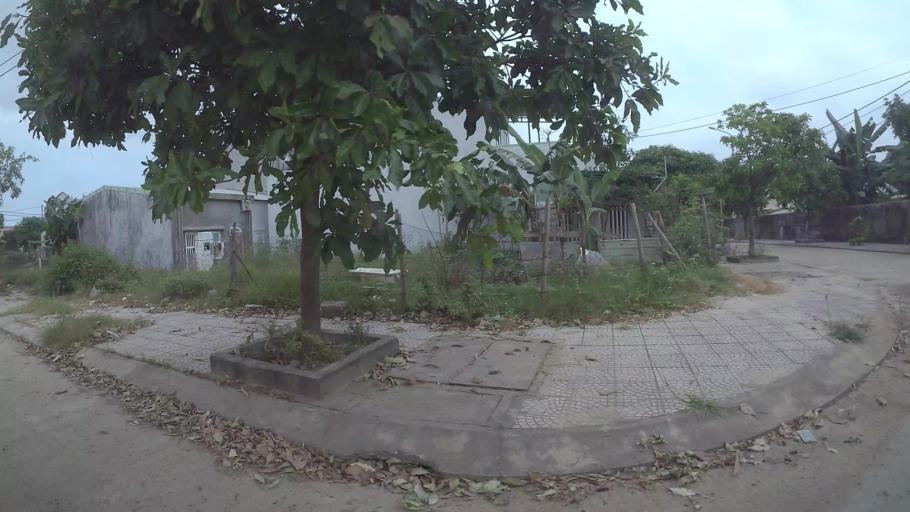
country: VN
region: Da Nang
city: Cam Le
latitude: 16.0337
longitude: 108.1763
